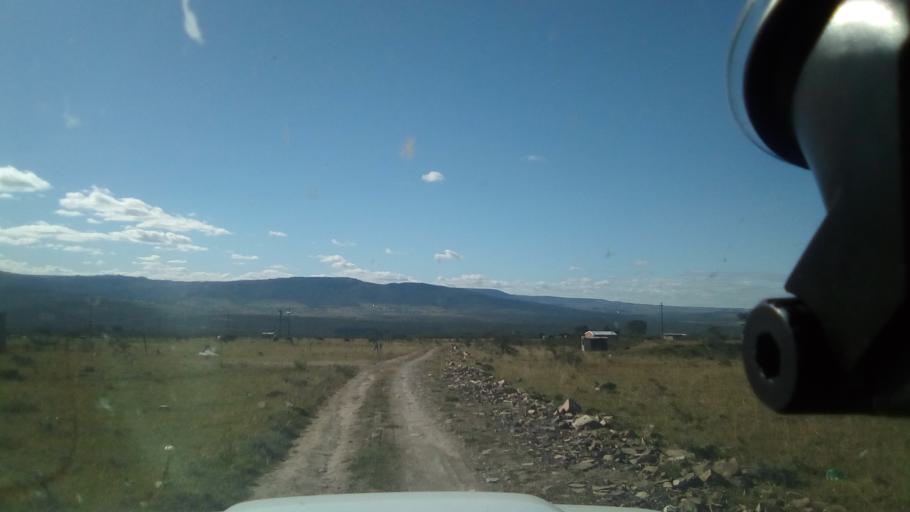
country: ZA
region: Eastern Cape
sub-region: Buffalo City Metropolitan Municipality
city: Bhisho
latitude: -32.7806
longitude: 27.3345
